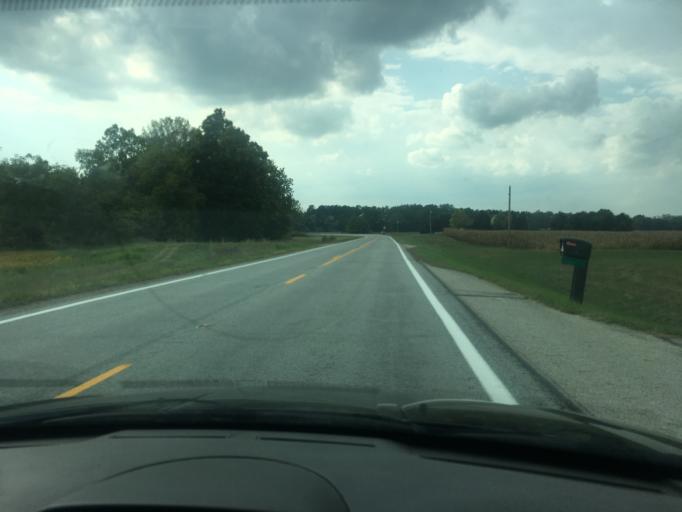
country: US
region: Ohio
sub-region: Champaign County
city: Urbana
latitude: 40.1573
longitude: -83.7801
